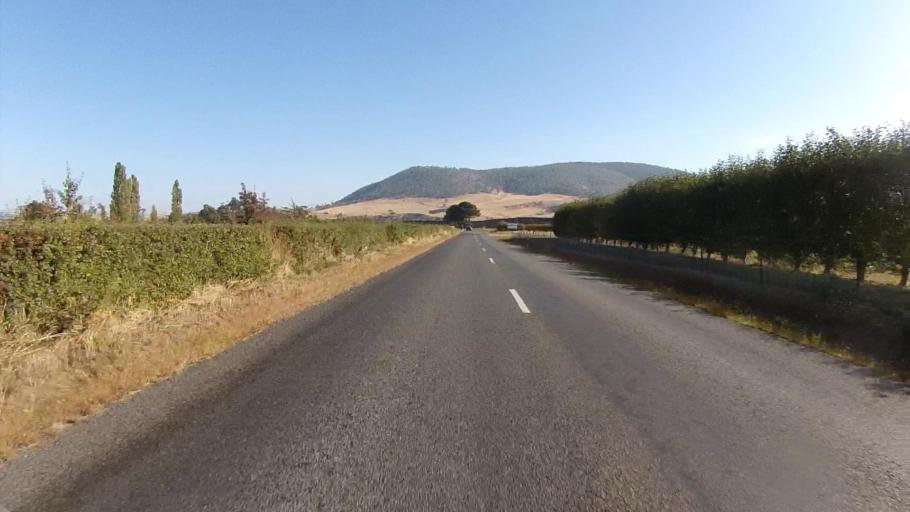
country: AU
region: Tasmania
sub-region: Derwent Valley
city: New Norfolk
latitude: -42.7457
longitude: 146.9721
